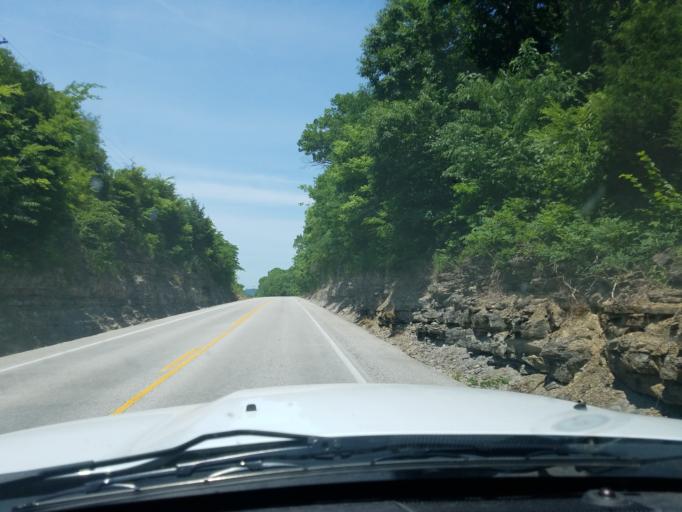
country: US
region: Tennessee
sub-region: Trousdale County
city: Hartsville
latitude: 36.4244
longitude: -86.2665
